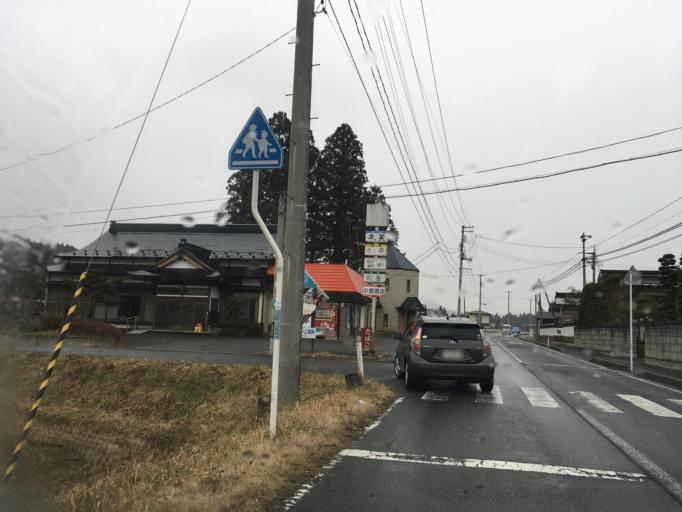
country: JP
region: Iwate
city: Ichinoseki
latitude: 38.8522
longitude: 140.9562
